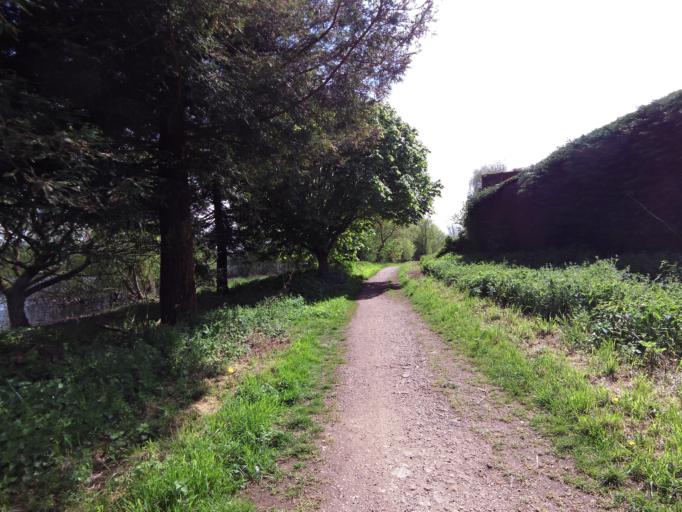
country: GB
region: England
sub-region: Essex
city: Mistley
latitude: 51.9885
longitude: 1.1157
